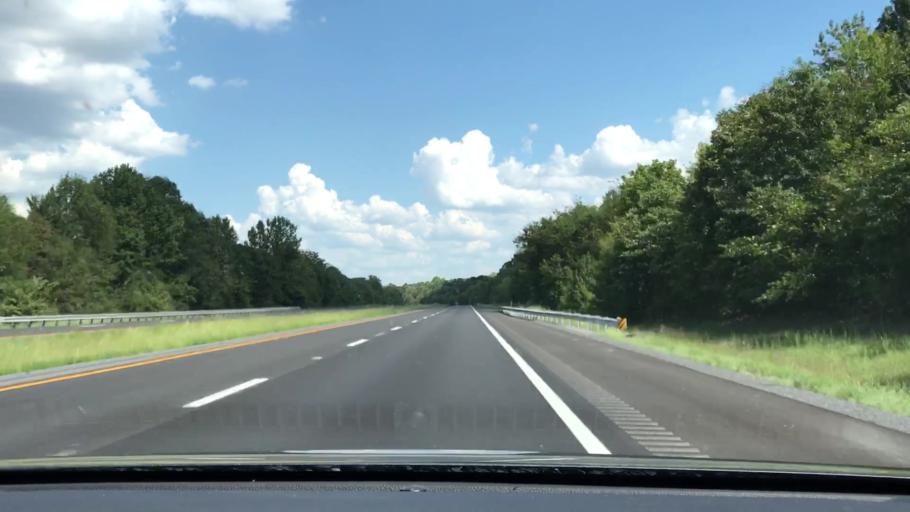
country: US
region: Kentucky
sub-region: Lyon County
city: Eddyville
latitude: 37.0931
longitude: -88.0490
